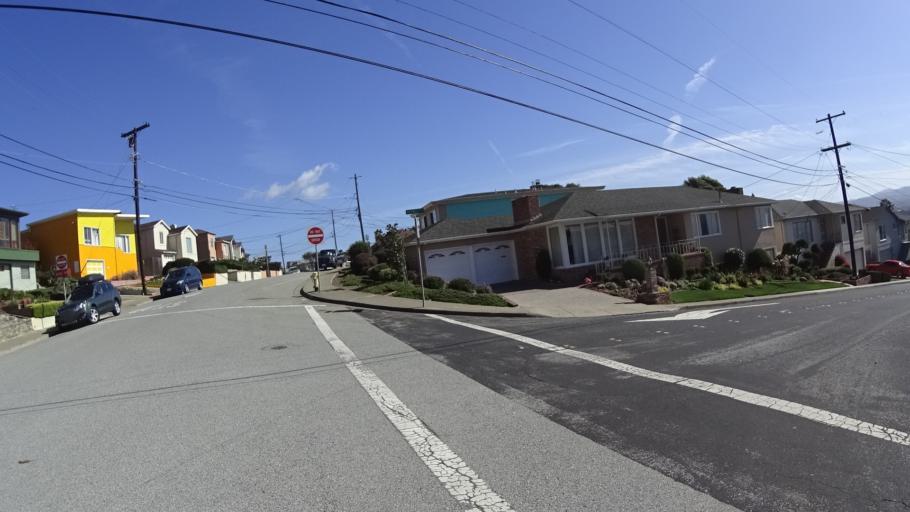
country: US
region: California
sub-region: San Mateo County
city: South San Francisco
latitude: 37.6618
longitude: -122.4211
